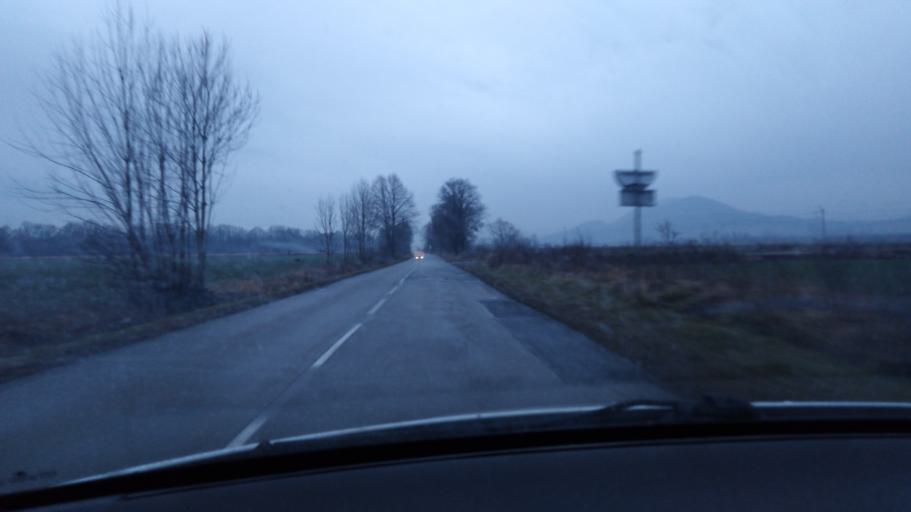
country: PL
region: Silesian Voivodeship
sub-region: Powiat zywiecki
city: Radziechowy
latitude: 49.6363
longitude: 19.1554
